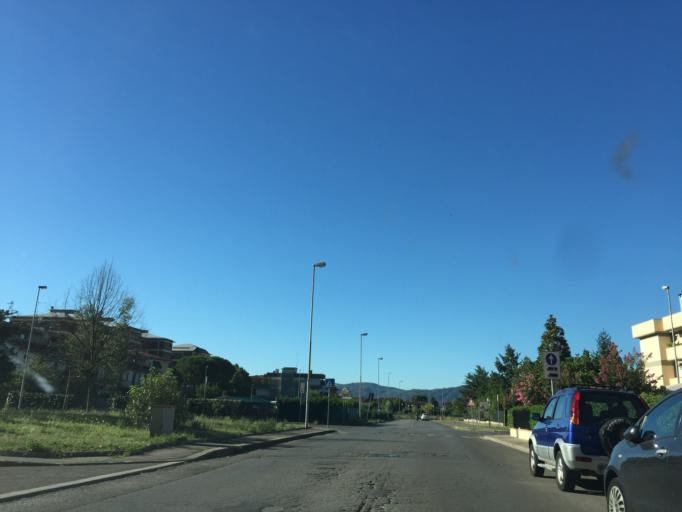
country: IT
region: Tuscany
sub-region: Provincia di Pistoia
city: Pistoia
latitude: 43.9361
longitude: 10.8975
